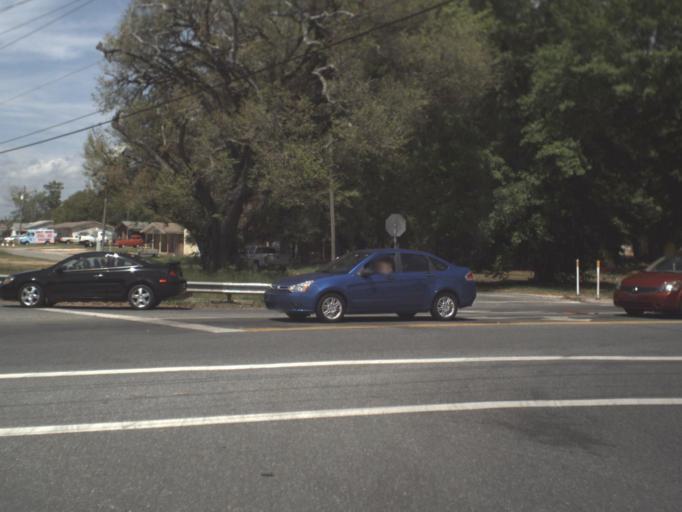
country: US
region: Florida
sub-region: Santa Rosa County
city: Pace
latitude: 30.6036
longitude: -87.1487
